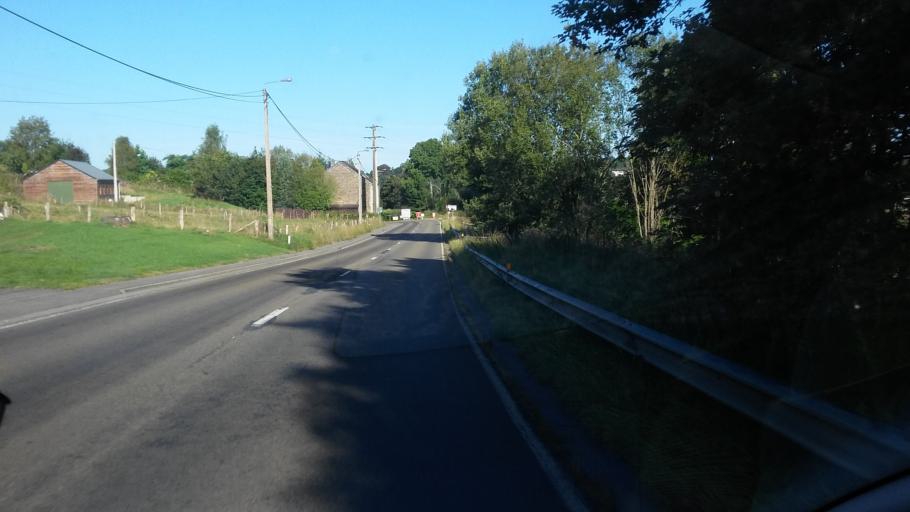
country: BE
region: Wallonia
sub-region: Province du Luxembourg
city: Neufchateau
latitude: 49.8383
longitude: 5.4490
